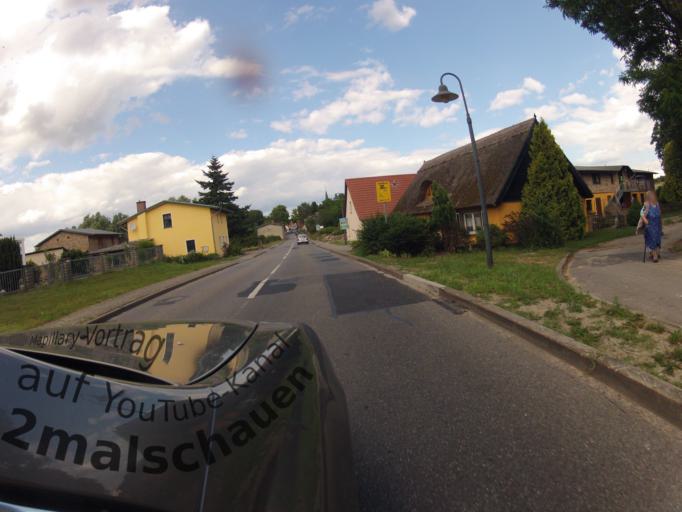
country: DE
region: Mecklenburg-Vorpommern
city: Seebad Heringsdorf
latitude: 53.8880
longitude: 14.1370
